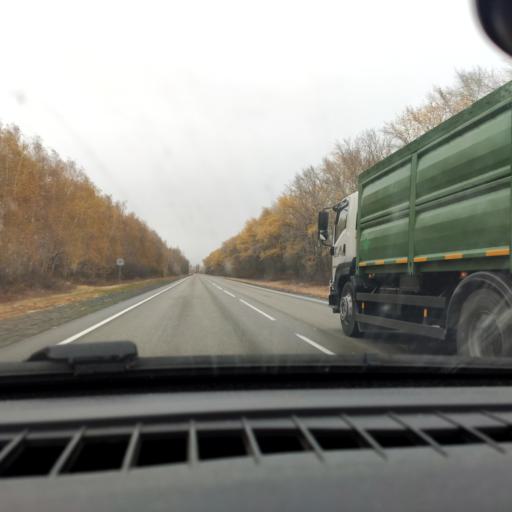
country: RU
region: Voronezj
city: Ostrogozhsk
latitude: 50.9938
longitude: 38.9988
